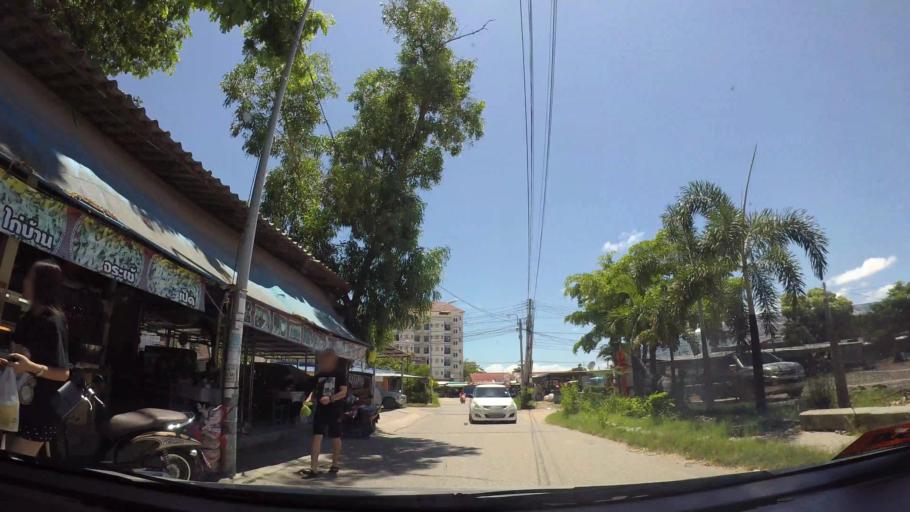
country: TH
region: Chon Buri
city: Phatthaya
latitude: 12.9238
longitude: 100.8915
